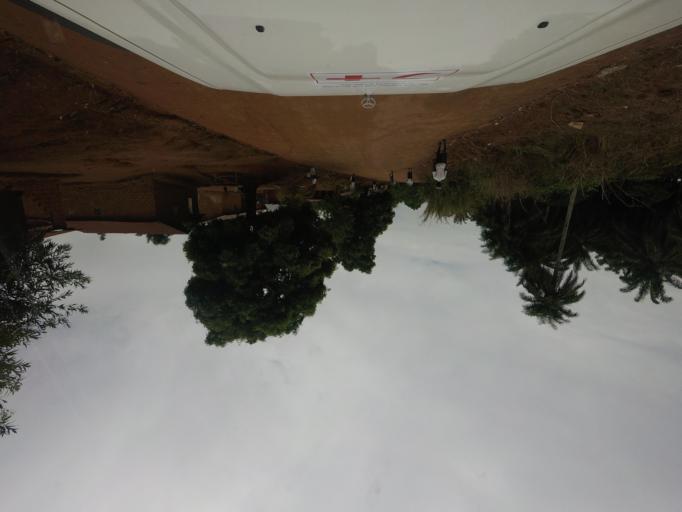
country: SL
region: Eastern Province
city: Buedu
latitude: 8.3476
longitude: -10.2065
